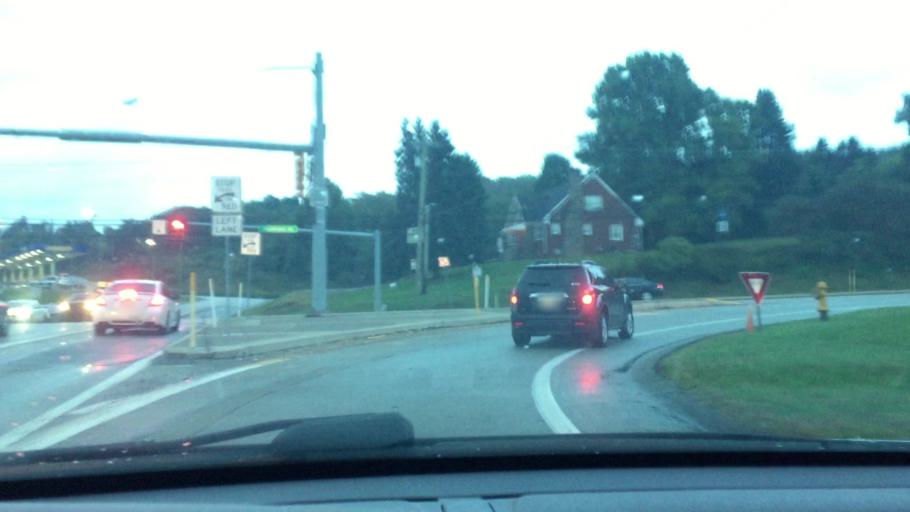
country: US
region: Pennsylvania
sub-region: Washington County
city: McGovern
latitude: 40.2119
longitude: -80.1966
